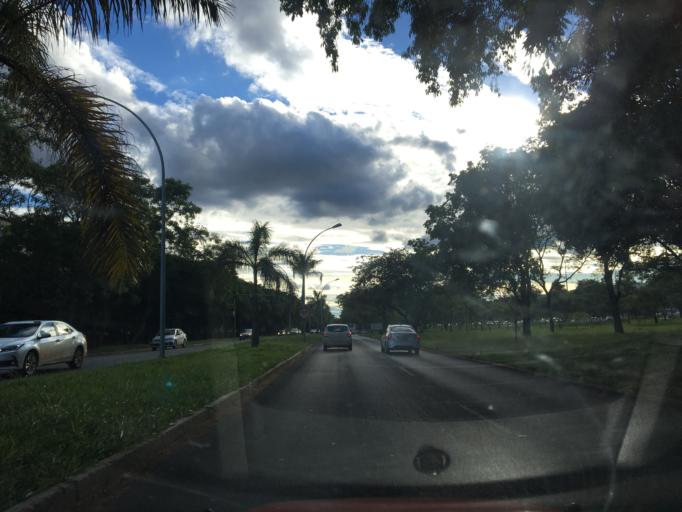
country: BR
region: Federal District
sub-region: Brasilia
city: Brasilia
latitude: -15.8275
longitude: -47.9143
